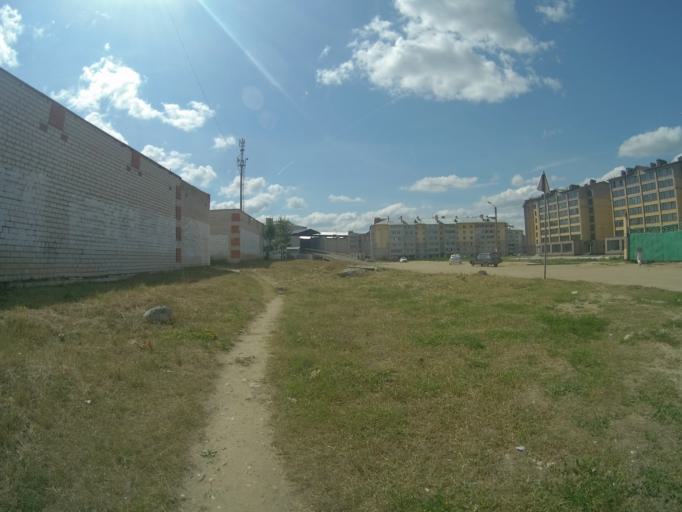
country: RU
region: Vladimir
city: Kommunar
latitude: 56.1080
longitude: 40.4393
